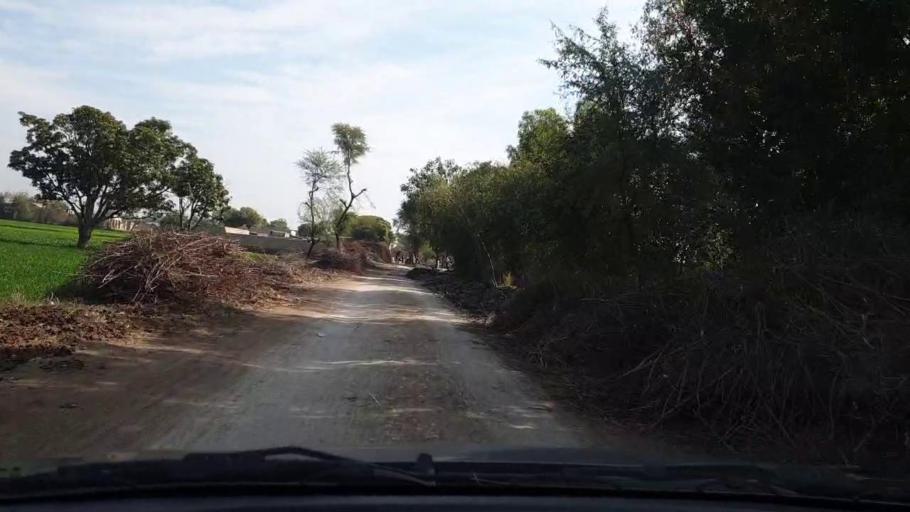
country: PK
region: Sindh
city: Jam Sahib
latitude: 26.2599
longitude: 68.7072
